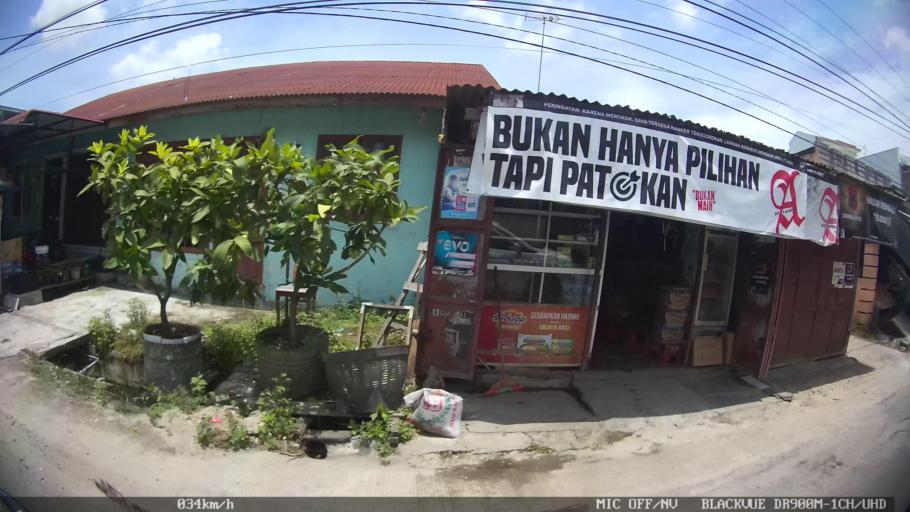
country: ID
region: North Sumatra
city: Percut
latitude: 3.5592
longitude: 98.8589
